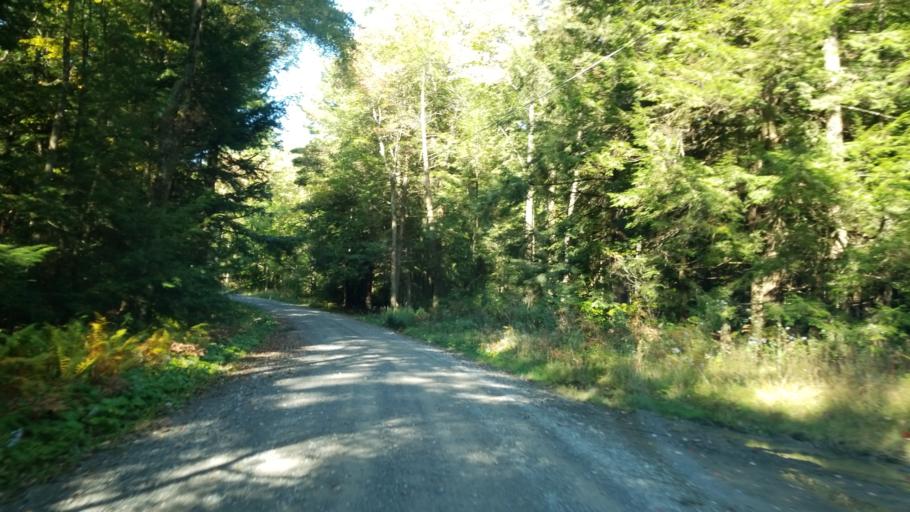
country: US
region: Pennsylvania
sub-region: Clearfield County
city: Hyde
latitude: 41.0888
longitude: -78.5354
